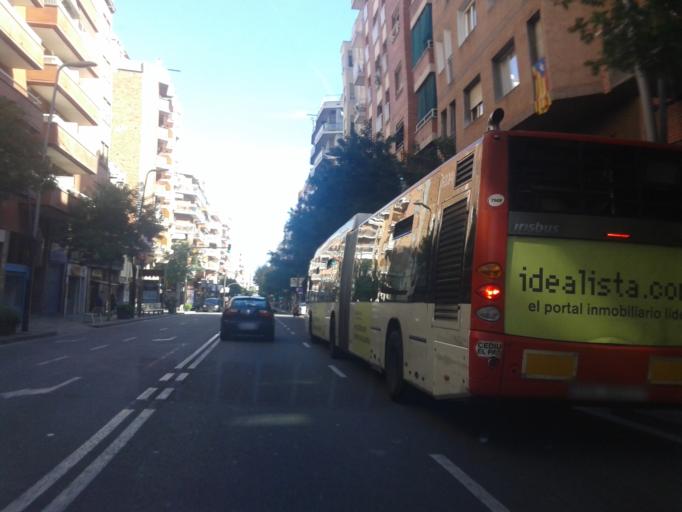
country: ES
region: Catalonia
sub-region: Provincia de Barcelona
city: les Corts
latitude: 41.3756
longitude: 2.1254
